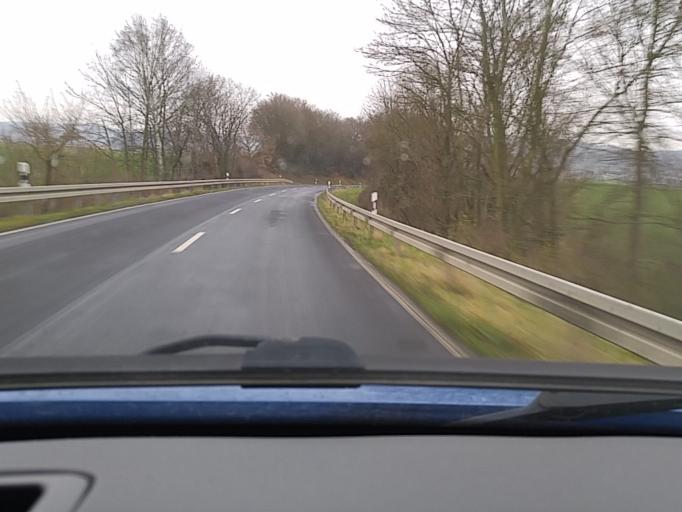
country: DE
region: Hesse
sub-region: Regierungsbezirk Darmstadt
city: Ranstadt
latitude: 50.3606
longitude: 8.9471
